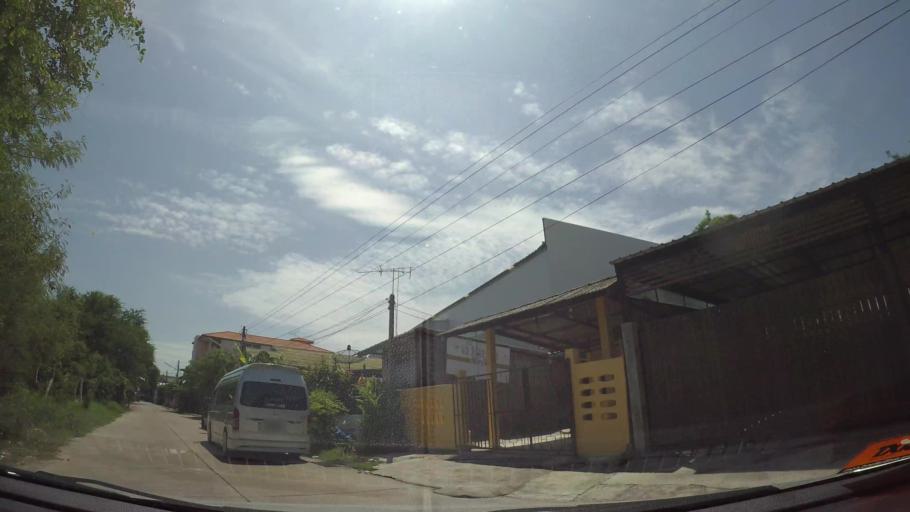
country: TH
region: Chon Buri
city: Chon Buri
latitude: 13.3167
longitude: 100.9567
